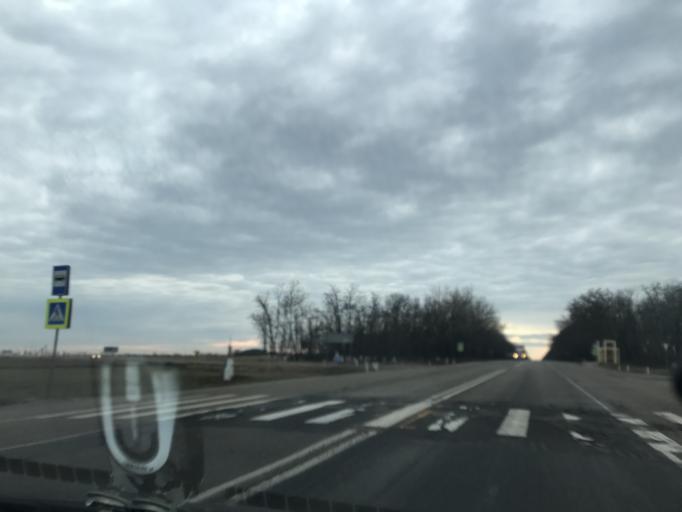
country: RU
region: Krasnodarskiy
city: Mirskoy
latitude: 45.5427
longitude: 40.4491
